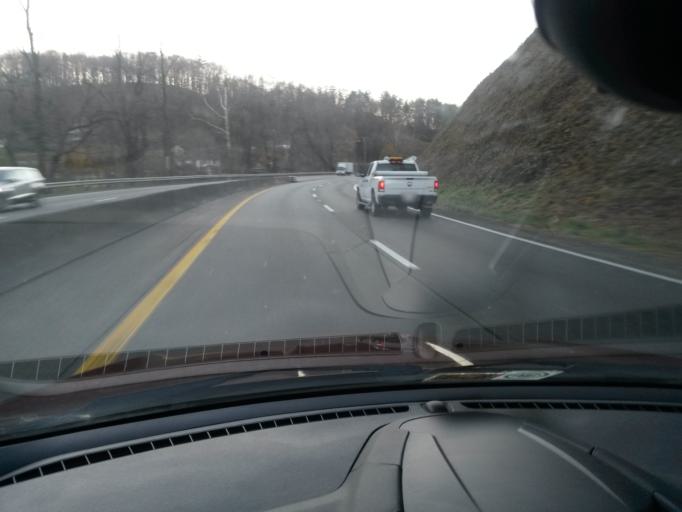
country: US
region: Virginia
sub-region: Roanoke County
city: Narrows
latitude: 37.1222
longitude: -79.9565
